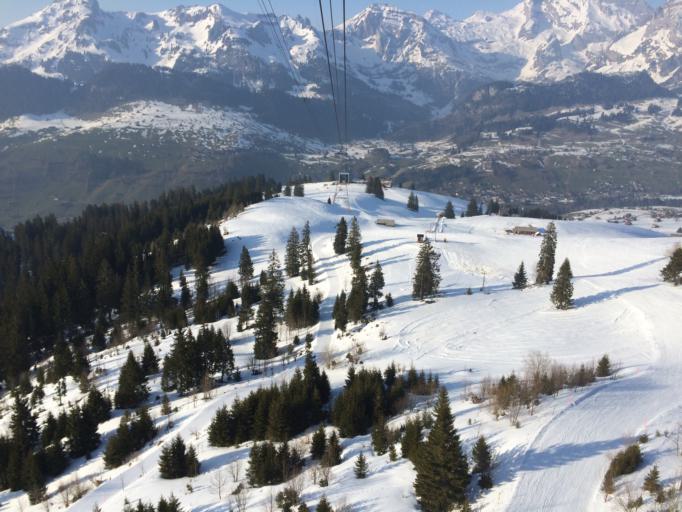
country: CH
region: Saint Gallen
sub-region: Wahlkreis Toggenburg
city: Wildhaus
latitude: 47.1776
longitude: 9.3120
